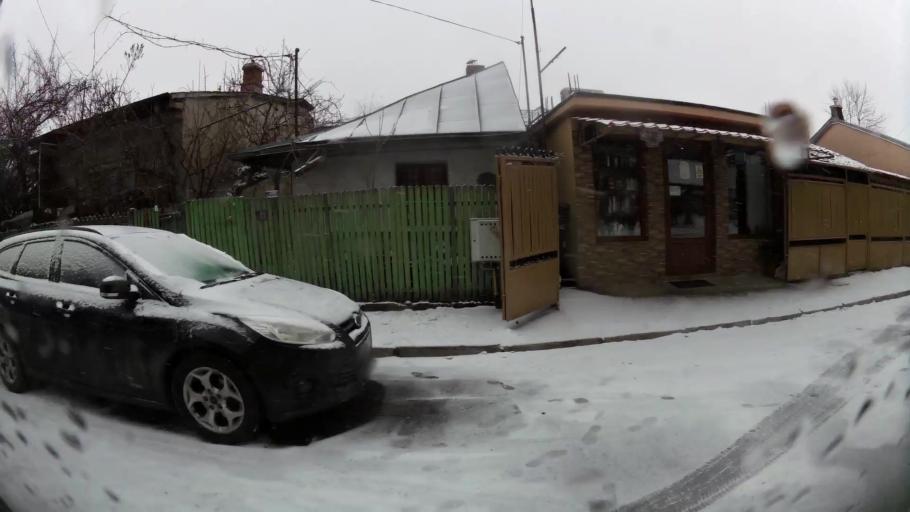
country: RO
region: Prahova
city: Ploiesti
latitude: 44.9289
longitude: 26.0083
